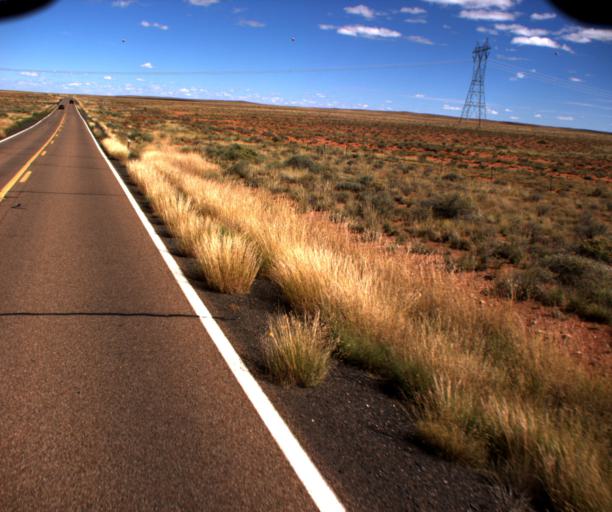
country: US
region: Arizona
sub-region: Navajo County
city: Holbrook
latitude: 34.7918
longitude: -110.2188
